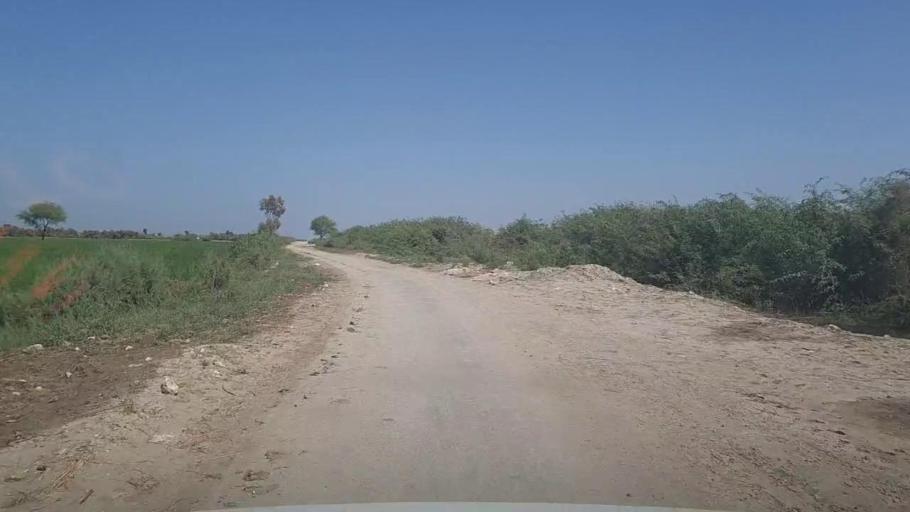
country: PK
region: Sindh
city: Kashmor
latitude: 28.2820
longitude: 69.4511
